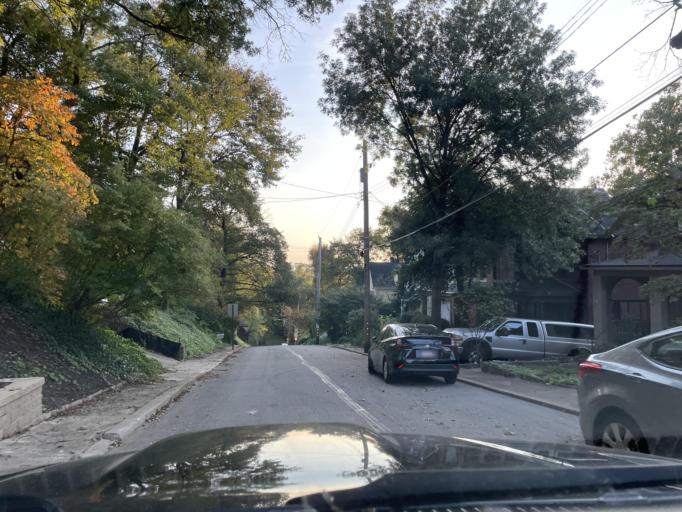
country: US
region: Pennsylvania
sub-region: Allegheny County
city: Edgewood
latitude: 40.4351
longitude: -79.8774
